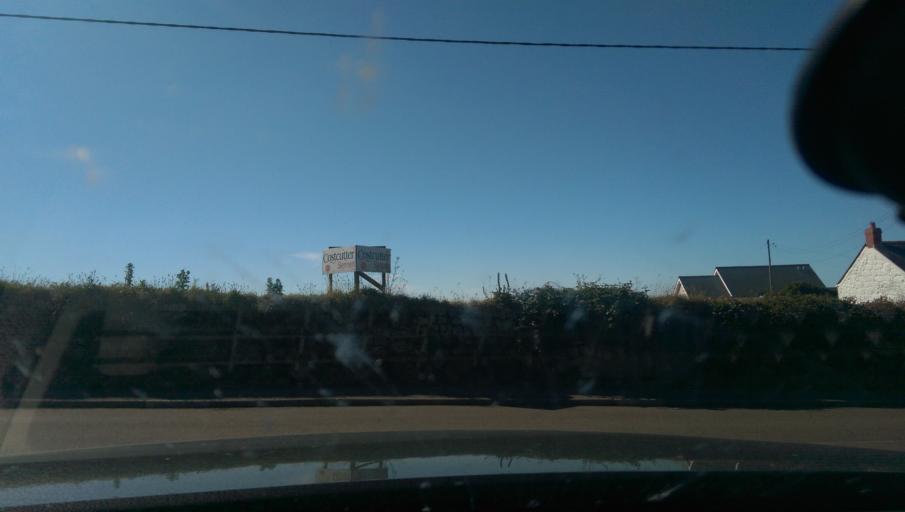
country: GB
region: England
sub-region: Cornwall
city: Sennen
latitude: 50.0740
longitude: -5.6930
